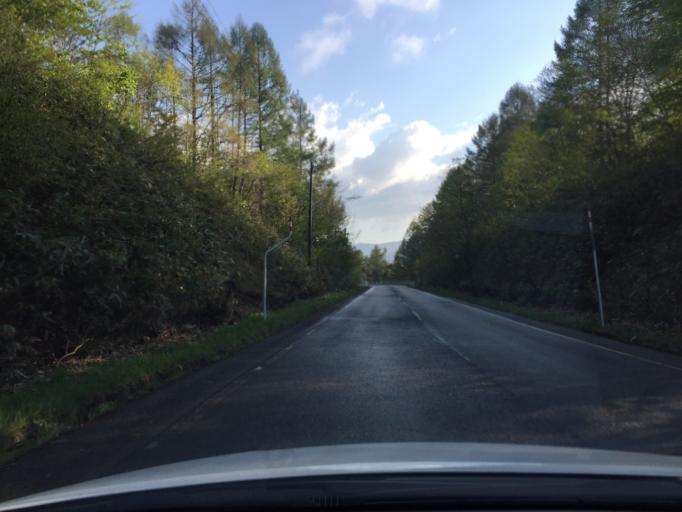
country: JP
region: Fukushima
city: Inawashiro
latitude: 37.6659
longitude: 140.0411
